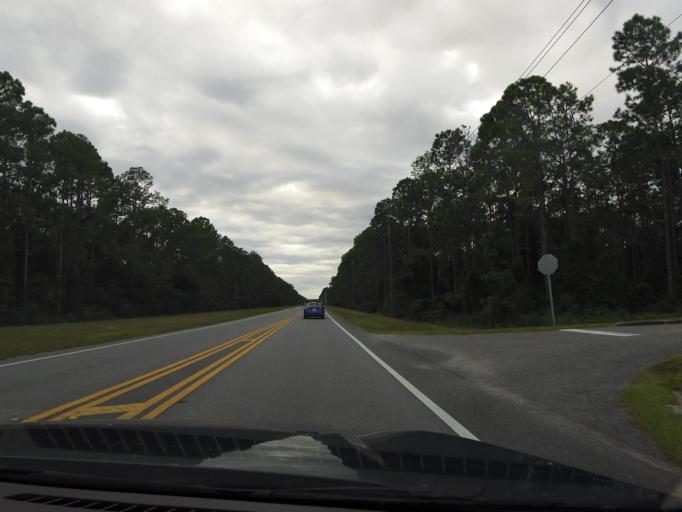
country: US
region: Florida
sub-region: Flagler County
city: Bunnell
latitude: 29.4973
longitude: -81.2464
